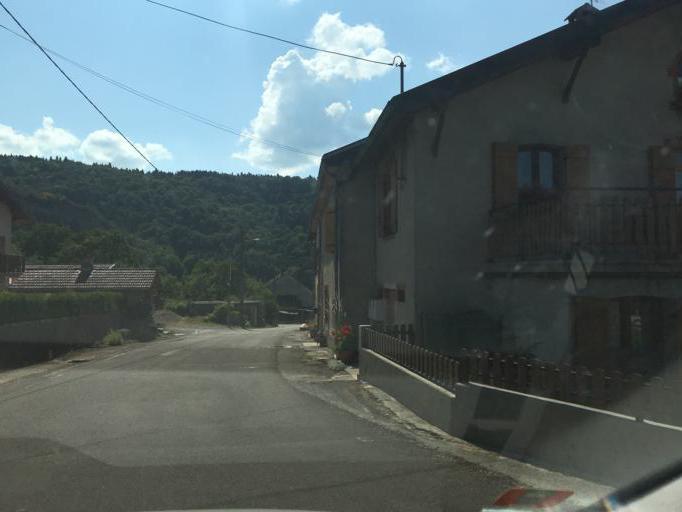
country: FR
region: Franche-Comte
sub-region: Departement du Jura
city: Moirans-en-Montagne
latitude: 46.4579
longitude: 5.7349
